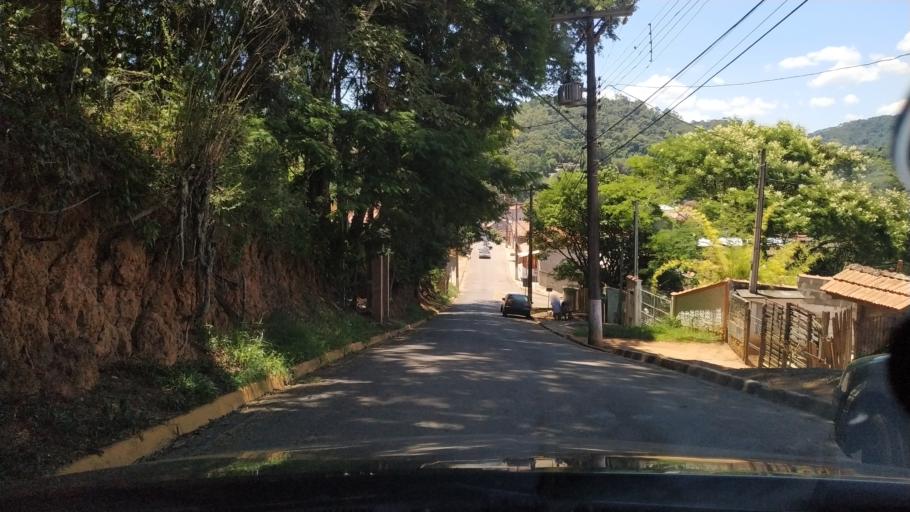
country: BR
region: Sao Paulo
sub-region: Campos Do Jordao
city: Campos do Jordao
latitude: -22.8281
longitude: -45.6668
